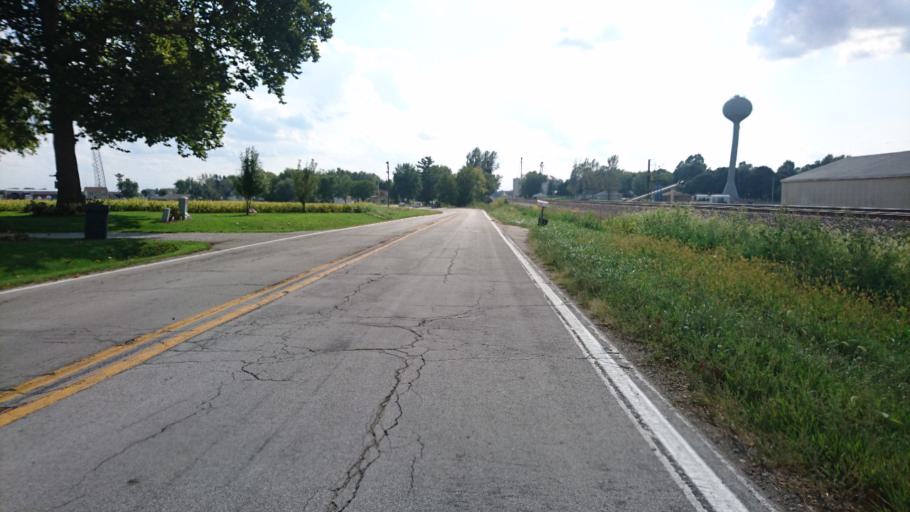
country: US
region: Illinois
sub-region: Logan County
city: Atlanta
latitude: 40.3189
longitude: -89.1645
